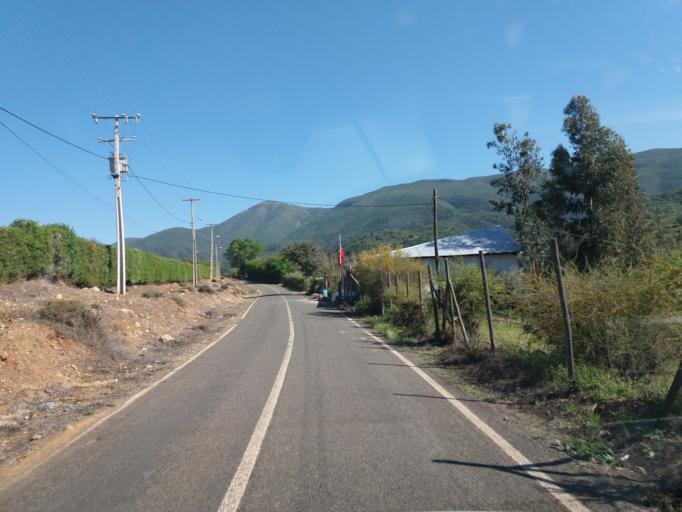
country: CL
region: Valparaiso
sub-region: Provincia de Quillota
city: Quillota
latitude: -32.8578
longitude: -71.2880
